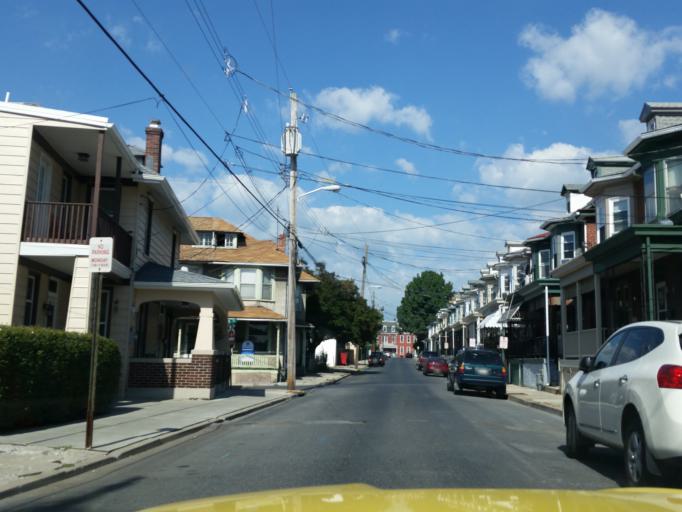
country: US
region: Pennsylvania
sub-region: Lebanon County
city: Lebanon
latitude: 40.3482
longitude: -76.4204
